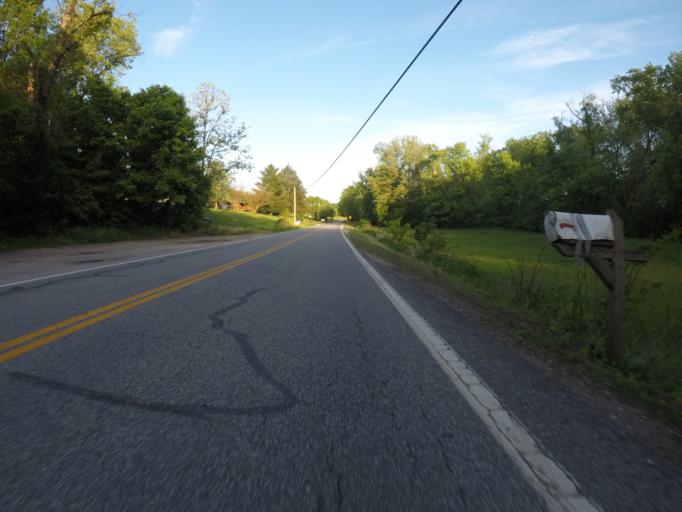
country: US
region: West Virginia
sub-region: Cabell County
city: Huntington
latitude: 38.4884
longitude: -82.4733
